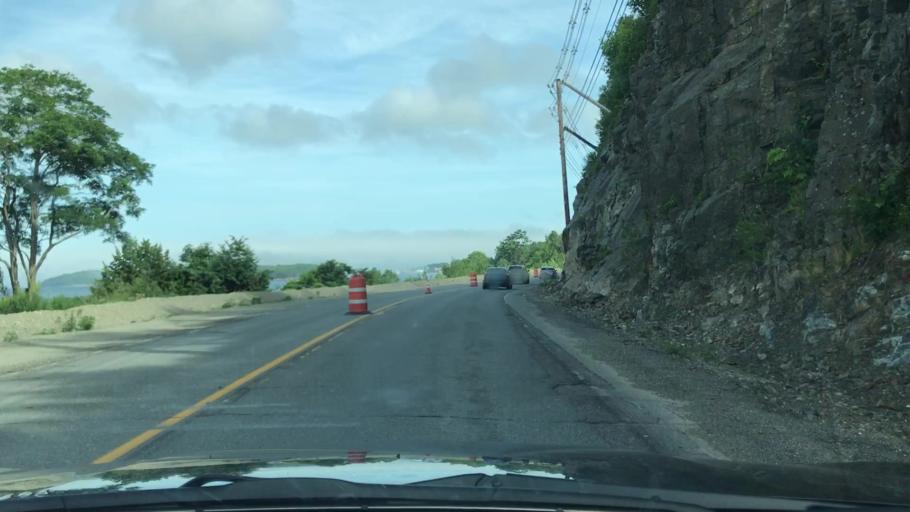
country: US
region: Maine
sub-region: Hancock County
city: Bar Harbor
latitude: 44.4074
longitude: -68.2376
